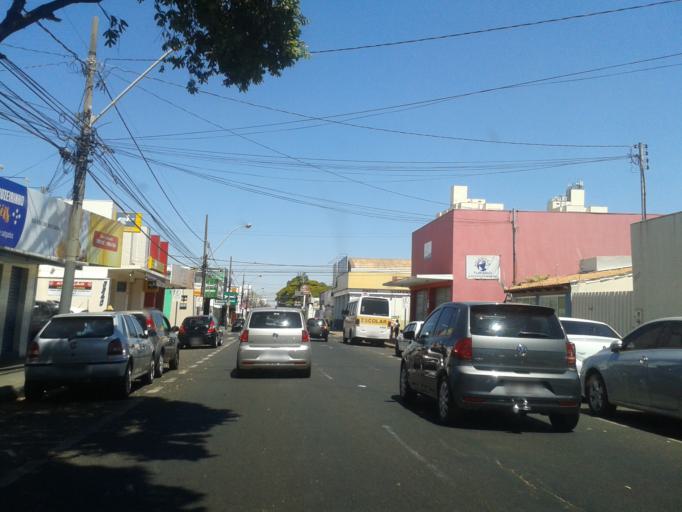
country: BR
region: Minas Gerais
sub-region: Uberlandia
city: Uberlandia
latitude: -18.8984
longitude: -48.2611
